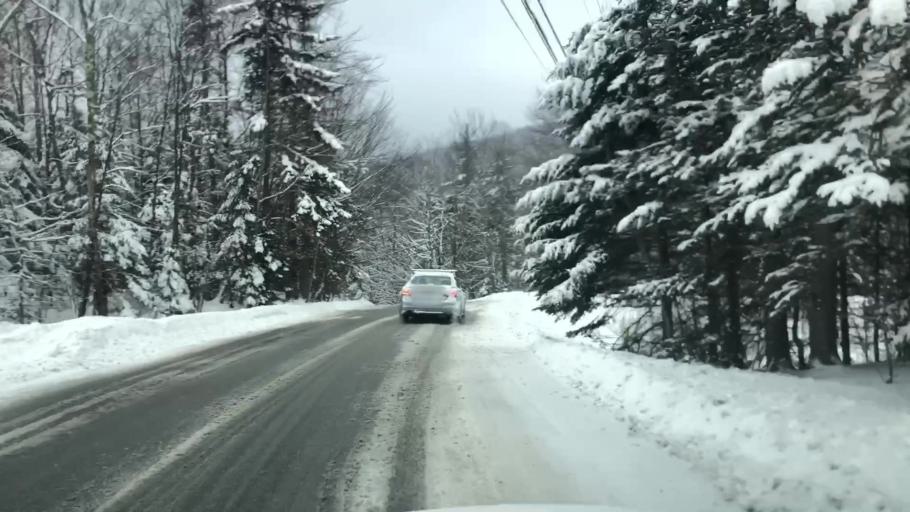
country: US
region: Vermont
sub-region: Rutland County
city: Rutland
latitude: 43.6493
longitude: -72.7846
